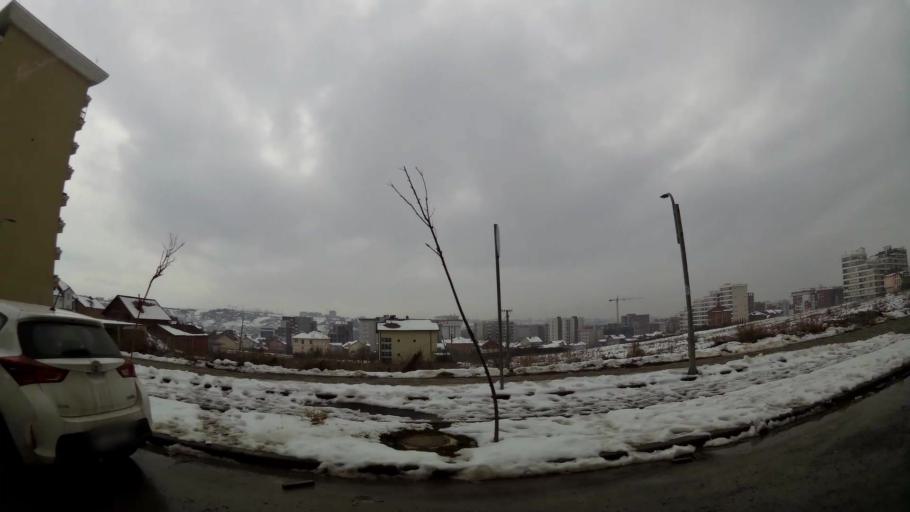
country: XK
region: Pristina
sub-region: Komuna e Prishtines
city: Pristina
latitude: 42.6493
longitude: 21.1805
